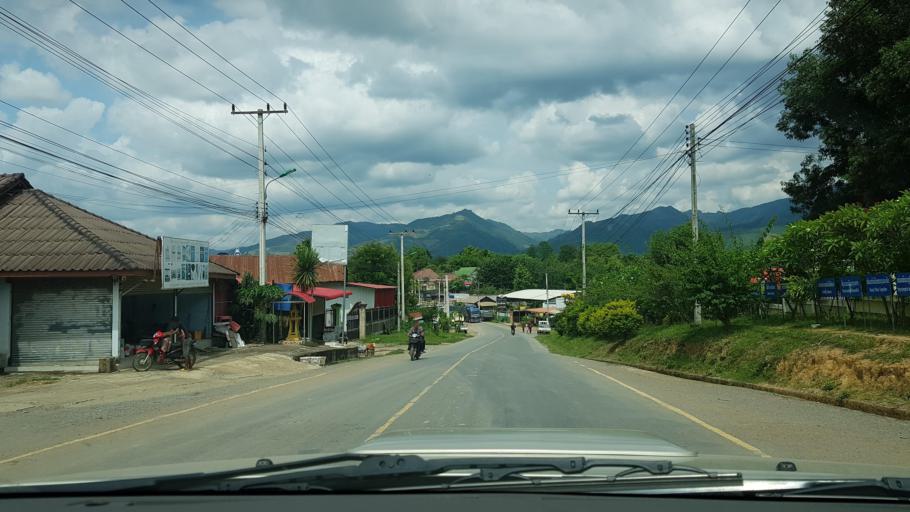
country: LA
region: Loungnamtha
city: Muang Nale
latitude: 20.1474
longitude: 101.4673
